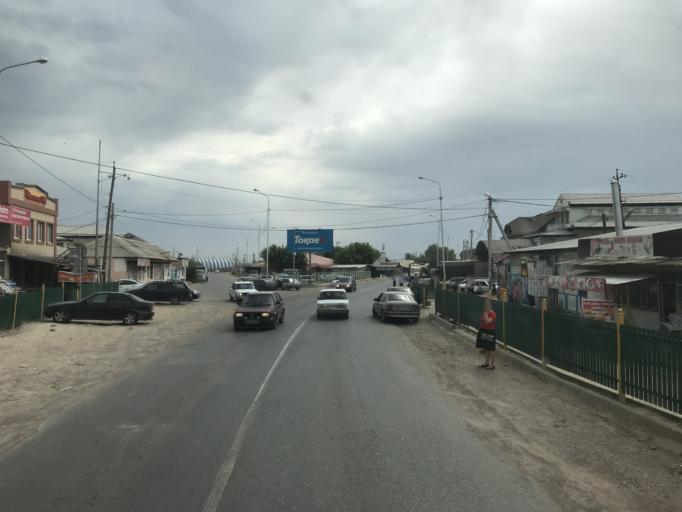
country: KZ
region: Ongtustik Qazaqstan
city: Saryaghash
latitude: 41.3388
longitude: 68.9513
